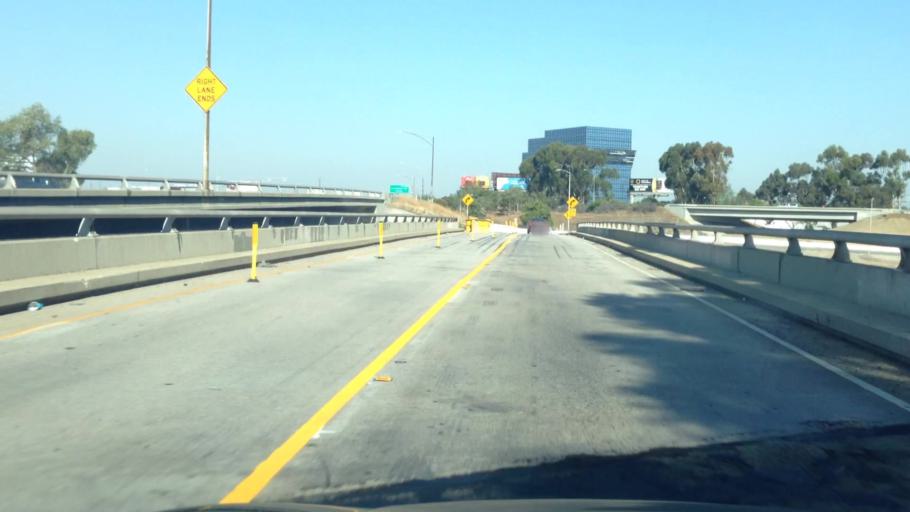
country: US
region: California
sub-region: Los Angeles County
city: Carson
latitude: 33.8571
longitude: -118.2843
